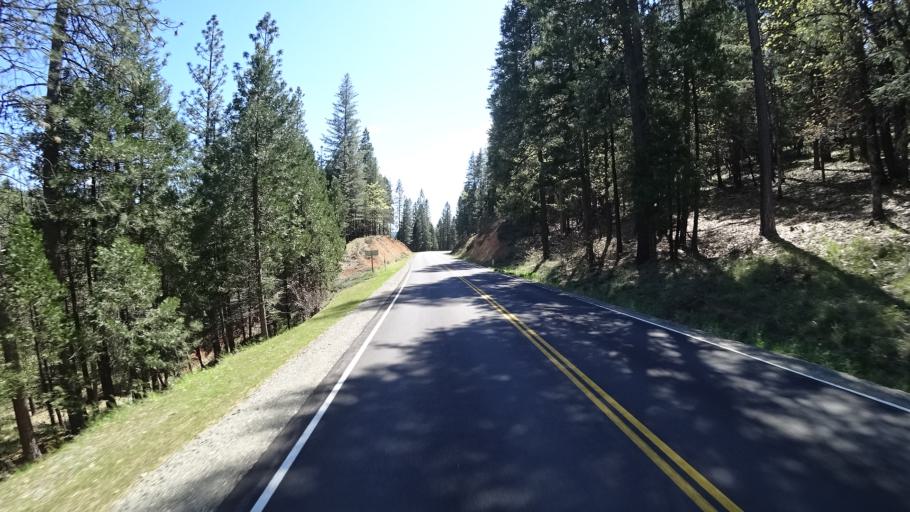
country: US
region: California
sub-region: Trinity County
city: Lewiston
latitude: 40.8815
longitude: -122.7982
